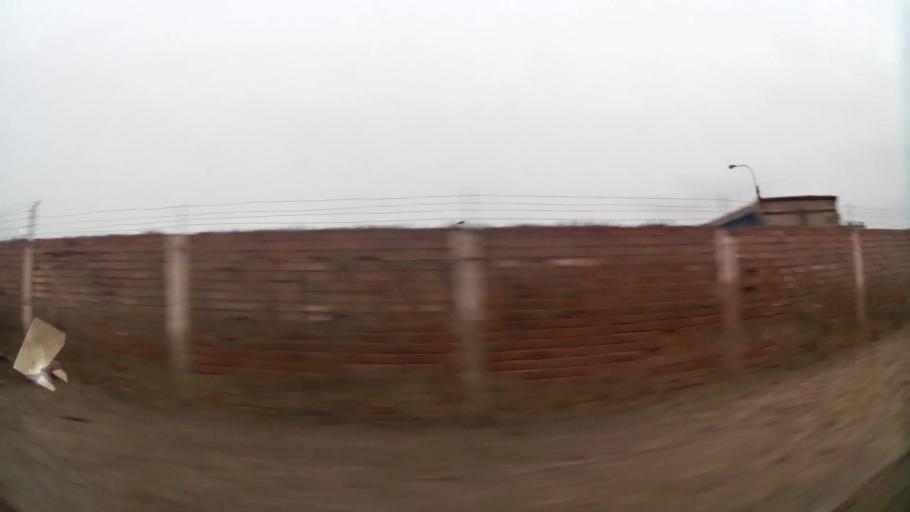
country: PE
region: Lima
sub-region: Lima
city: Surco
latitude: -12.1627
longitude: -76.9702
